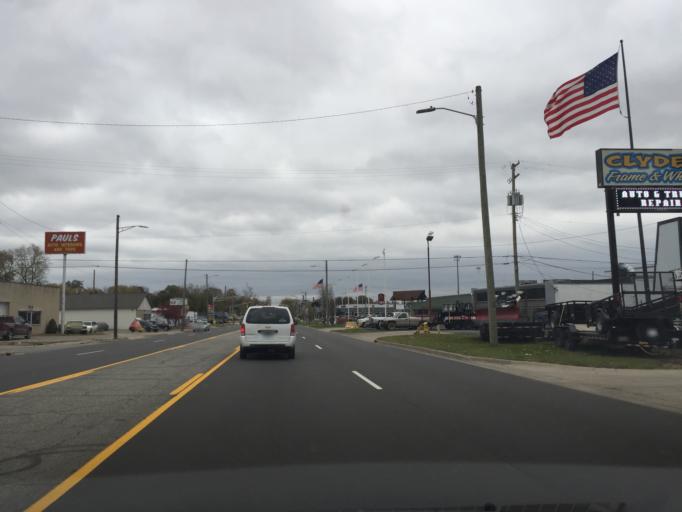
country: US
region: Michigan
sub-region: Oakland County
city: Pontiac
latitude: 42.6545
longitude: -83.3131
